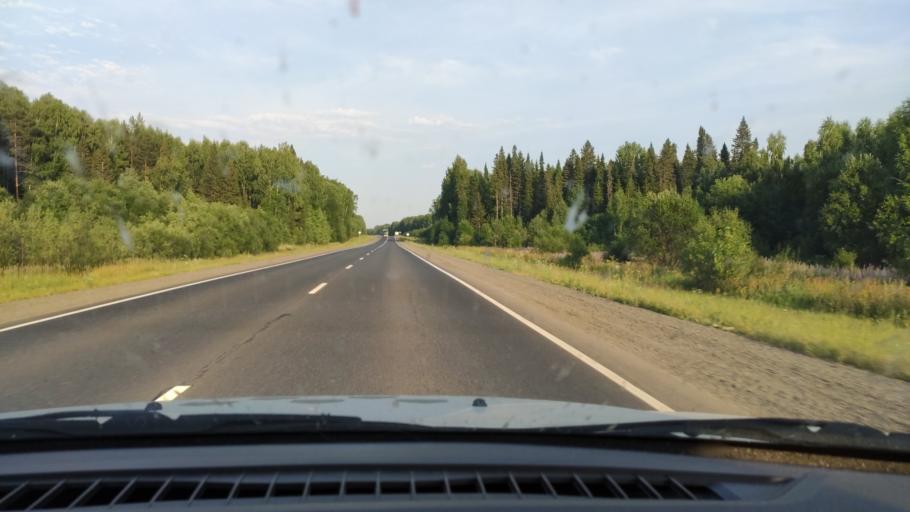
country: RU
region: Perm
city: Zyukayka
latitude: 58.3780
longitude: 54.6234
